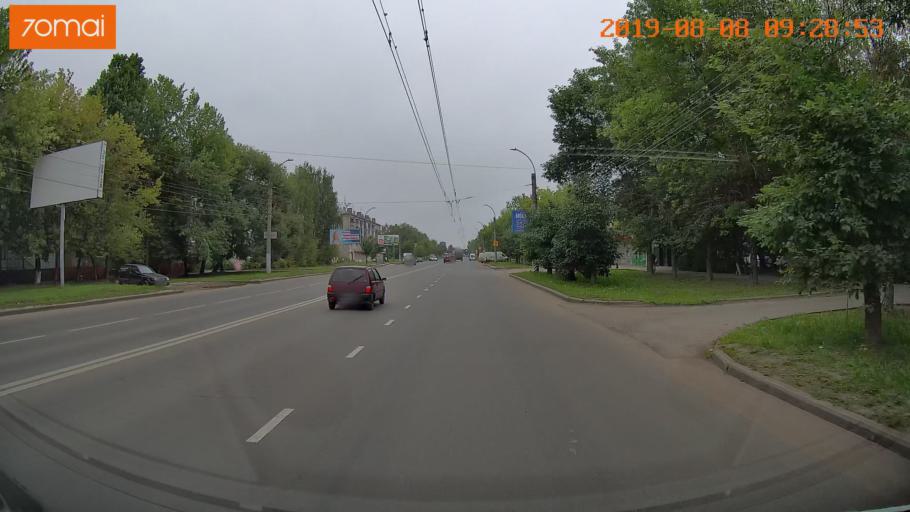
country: RU
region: Ivanovo
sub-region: Gorod Ivanovo
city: Ivanovo
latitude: 56.9672
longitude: 41.0082
